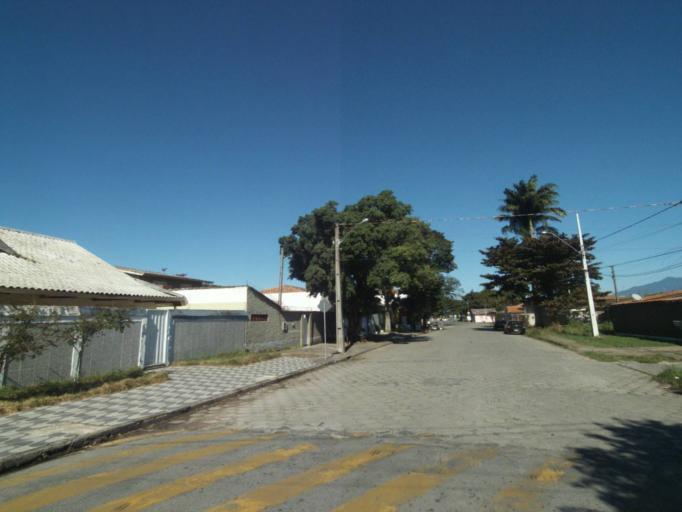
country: BR
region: Parana
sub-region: Paranagua
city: Paranagua
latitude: -25.5294
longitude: -48.5262
